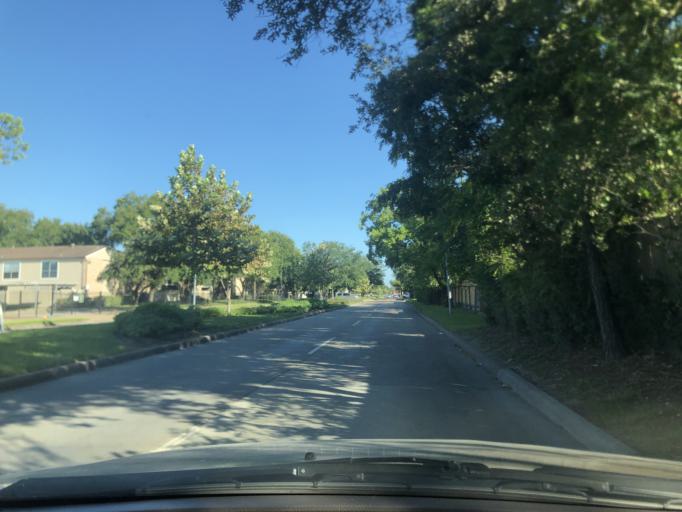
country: US
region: Texas
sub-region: Harris County
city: Bunker Hill Village
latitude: 29.7432
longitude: -95.5719
